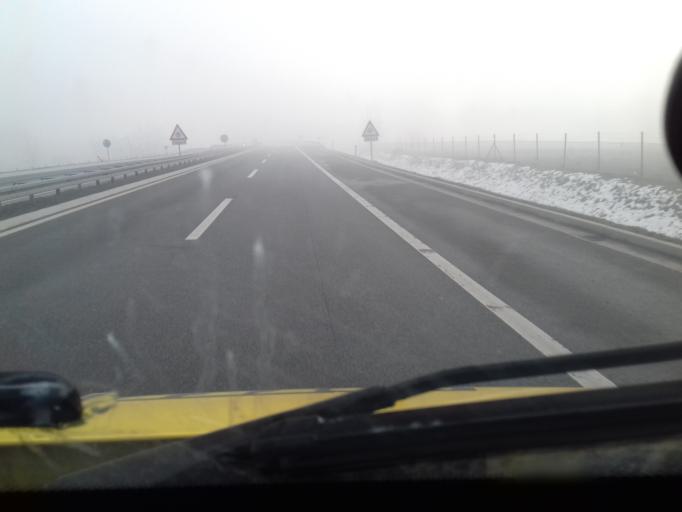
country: BA
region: Federation of Bosnia and Herzegovina
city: Ilijas
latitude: 43.9391
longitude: 18.2734
